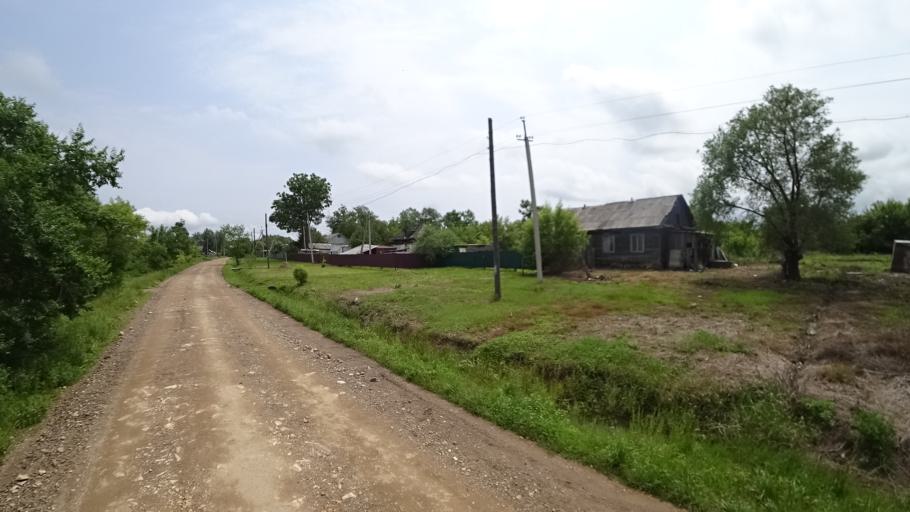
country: RU
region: Primorskiy
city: Novosysoyevka
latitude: 44.2391
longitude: 133.3586
